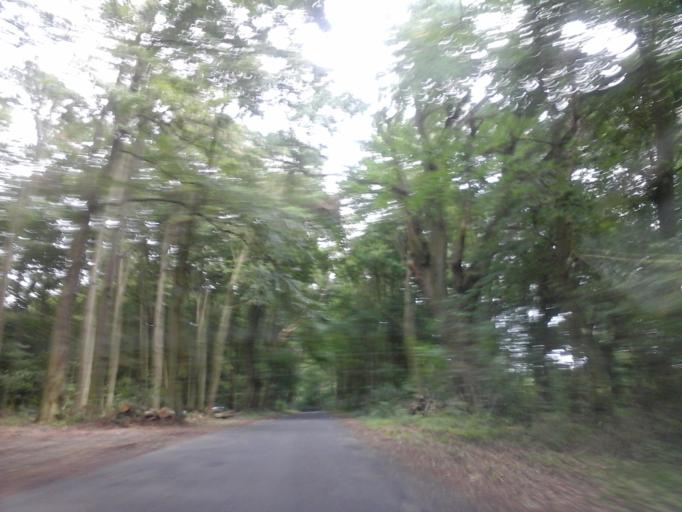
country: PL
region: West Pomeranian Voivodeship
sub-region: Powiat stargardzki
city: Marianowo
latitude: 53.3358
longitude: 15.2015
